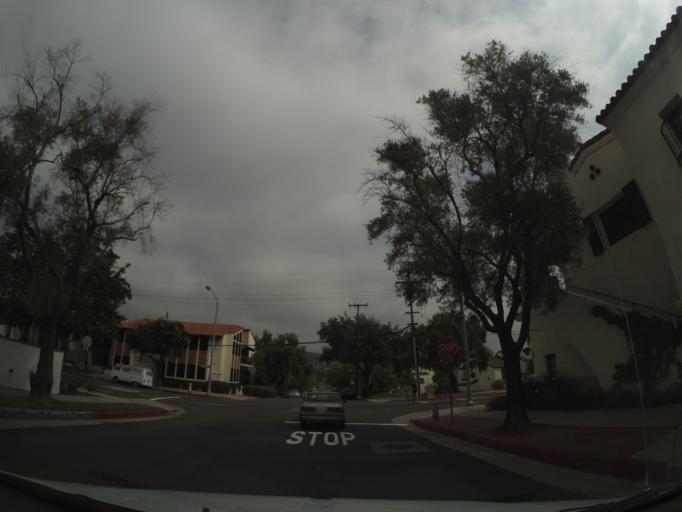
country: US
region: California
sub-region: Santa Barbara County
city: Santa Barbara
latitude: 34.4226
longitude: -119.6963
